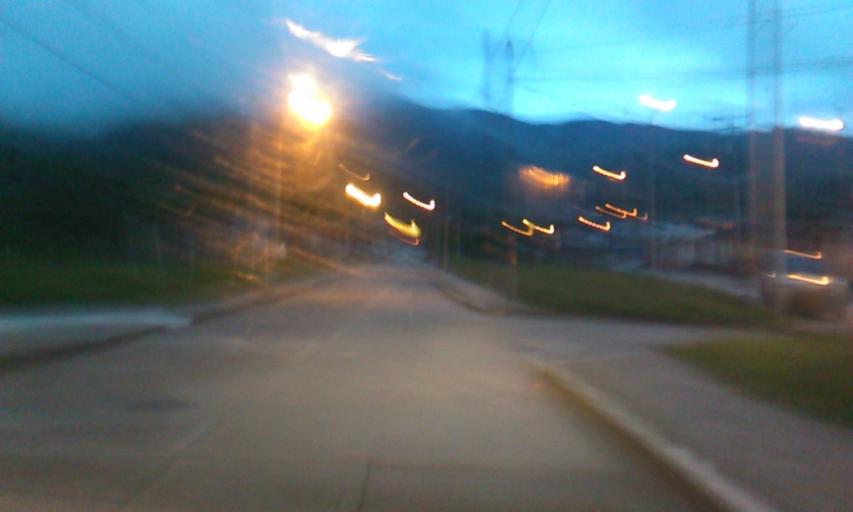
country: CO
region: Quindio
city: Cordoba
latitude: 4.3929
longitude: -75.6888
